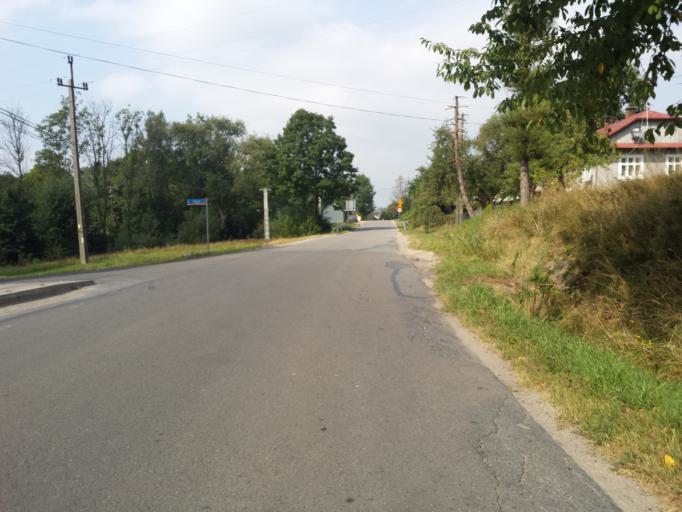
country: PL
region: Subcarpathian Voivodeship
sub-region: Powiat rzeszowski
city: Blazowa
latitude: 49.8562
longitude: 22.1318
